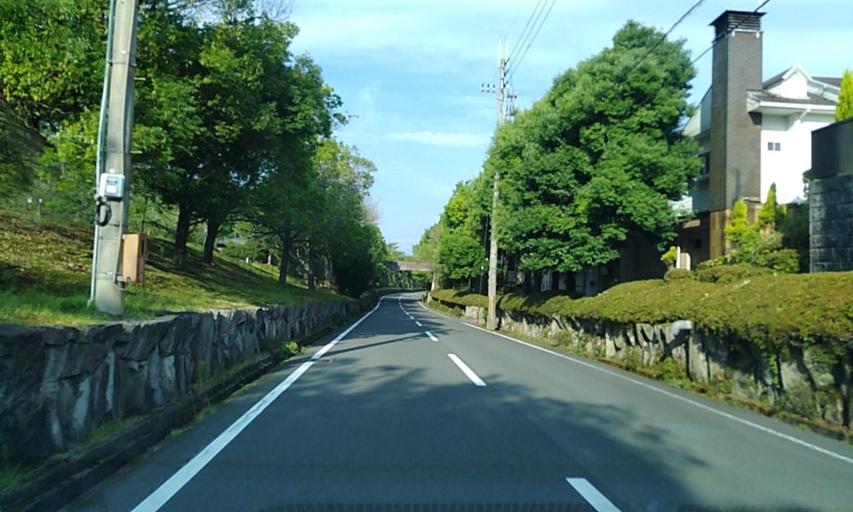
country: JP
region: Hyogo
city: Sasayama
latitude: 35.1625
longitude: 135.3713
